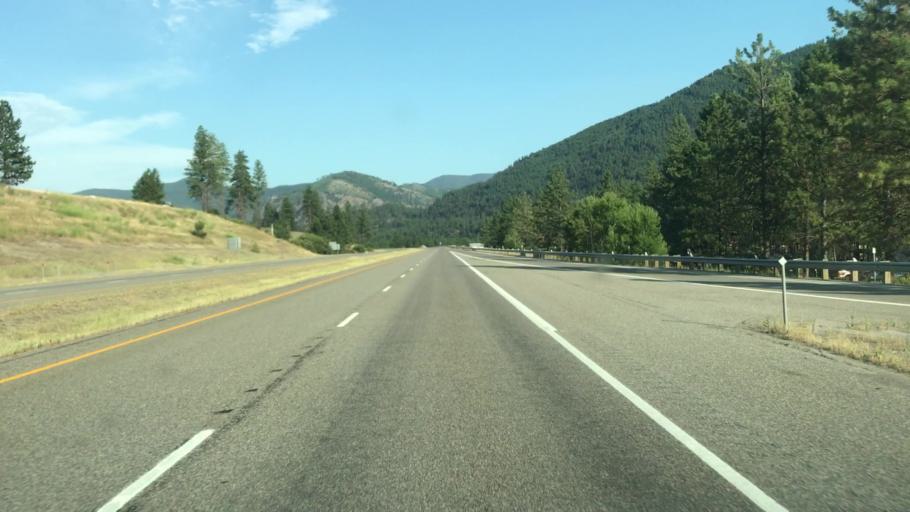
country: US
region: Montana
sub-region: Missoula County
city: Frenchtown
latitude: 47.0048
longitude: -114.4921
